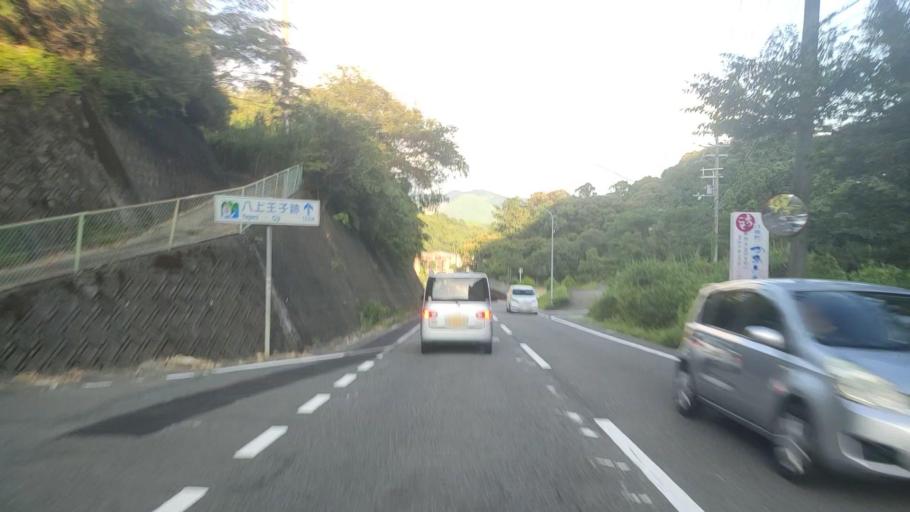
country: JP
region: Wakayama
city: Tanabe
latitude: 33.7271
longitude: 135.4390
